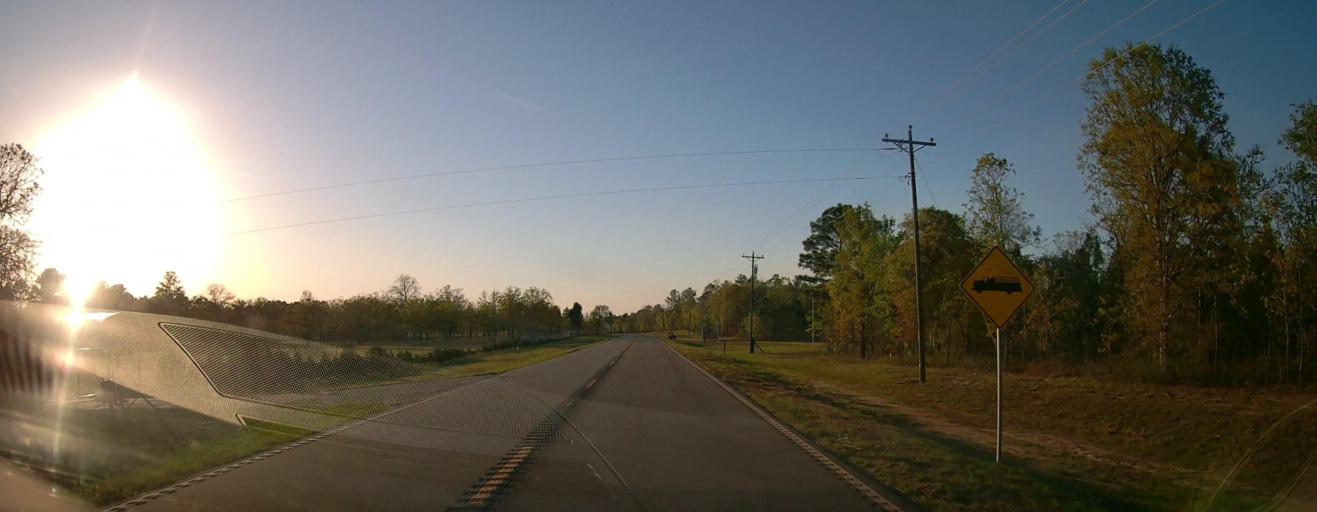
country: US
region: Georgia
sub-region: Talbot County
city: Talbotton
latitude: 32.5238
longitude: -84.4745
